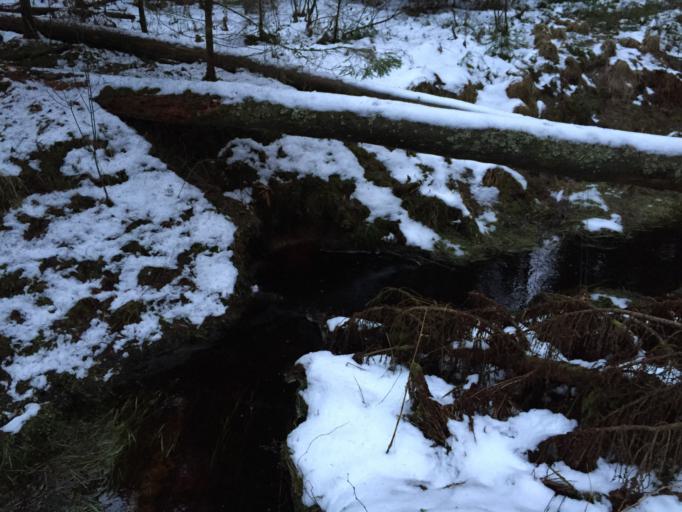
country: LV
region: Garkalne
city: Garkalne
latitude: 56.9646
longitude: 24.4717
